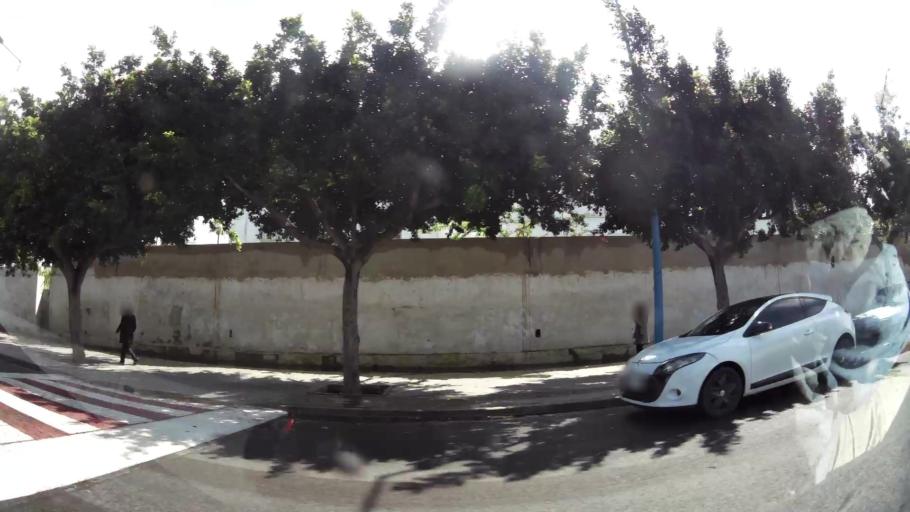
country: MA
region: Grand Casablanca
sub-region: Casablanca
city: Casablanca
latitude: 33.5761
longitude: -7.6206
